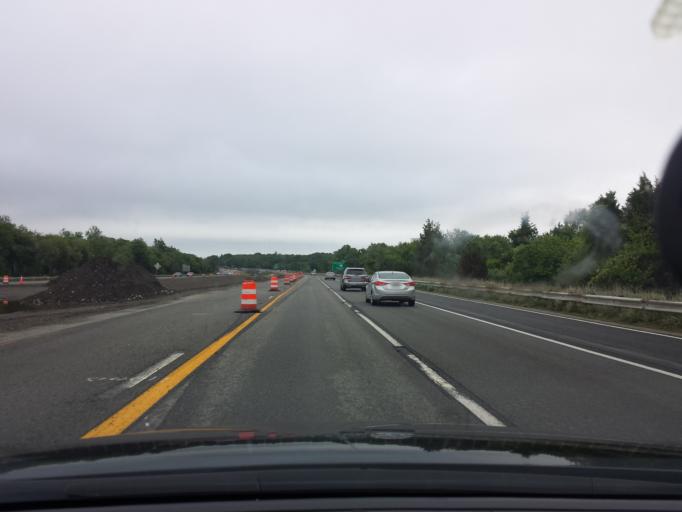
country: US
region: Massachusetts
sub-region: Bristol County
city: Ocean Grove
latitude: 41.7404
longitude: -71.2085
